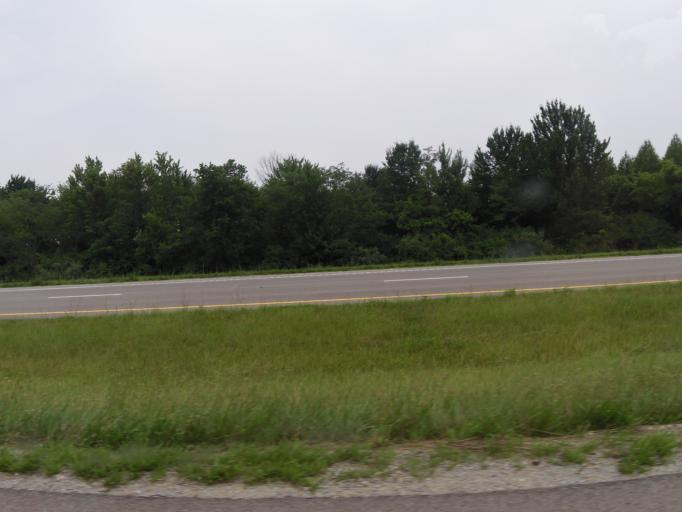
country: US
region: Ohio
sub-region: Warren County
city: Waynesville
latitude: 39.5112
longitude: -84.0275
